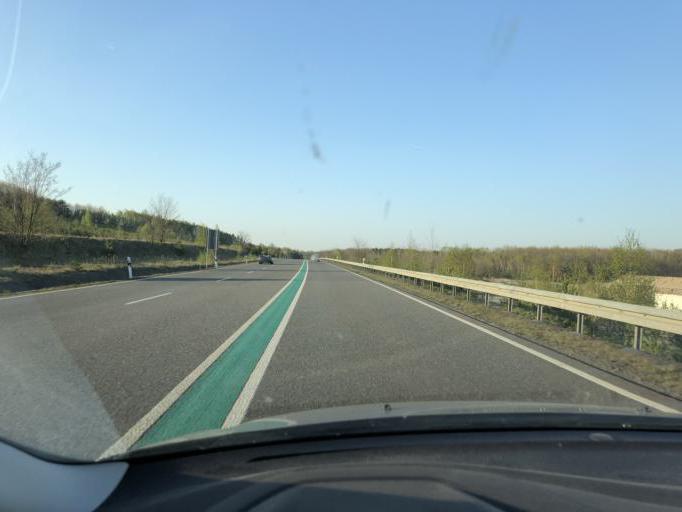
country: DE
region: Brandenburg
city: Senftenberg
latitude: 51.5173
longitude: 13.9621
